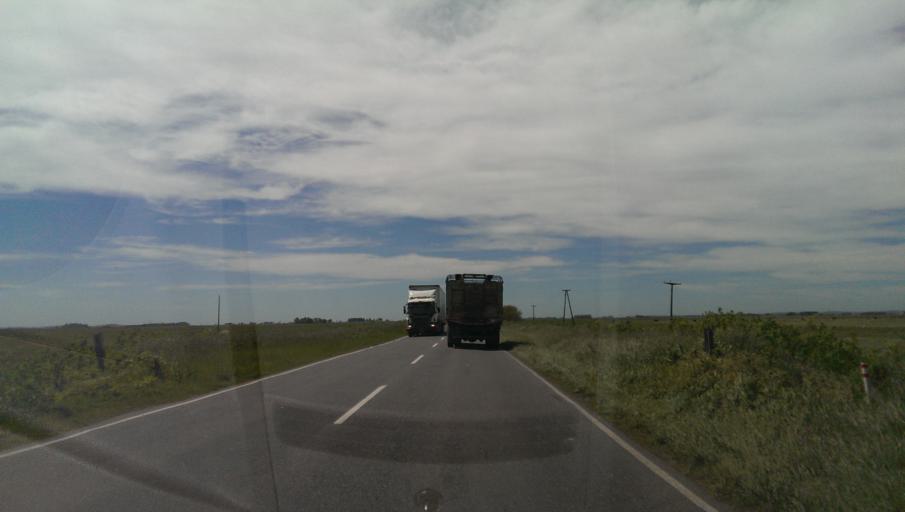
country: AR
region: Buenos Aires
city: Olavarria
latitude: -37.0725
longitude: -60.4731
